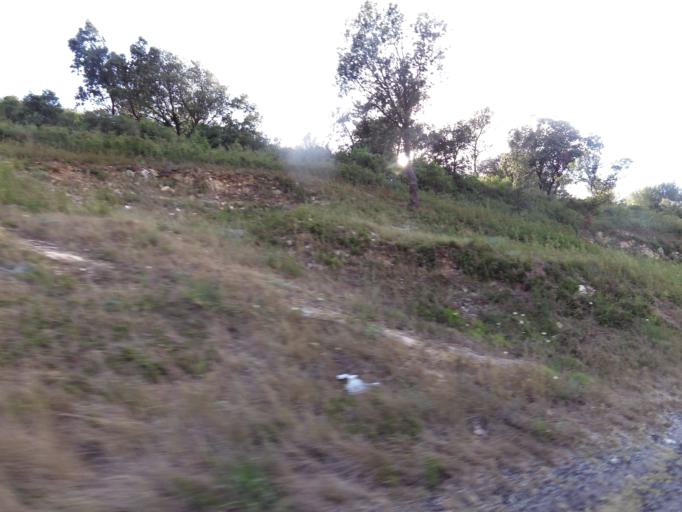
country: FR
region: Languedoc-Roussillon
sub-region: Departement du Gard
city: Congenies
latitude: 43.7984
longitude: 4.1604
